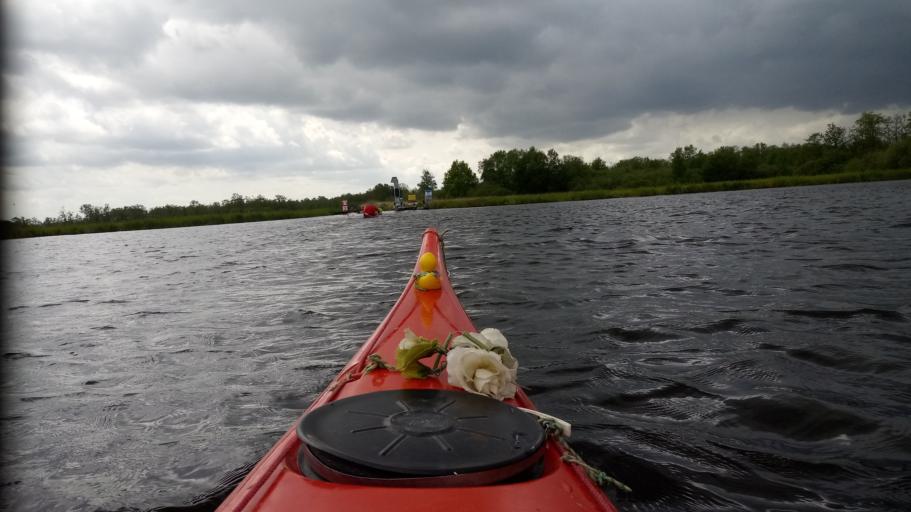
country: NL
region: Overijssel
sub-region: Gemeente Steenwijkerland
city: Sint Jansklooster
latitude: 52.7042
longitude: 6.0073
